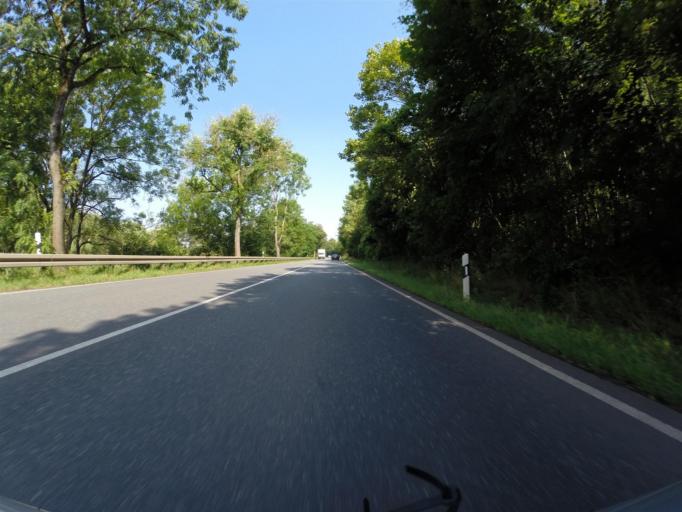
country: DE
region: Hesse
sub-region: Regierungsbezirk Kassel
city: Grossalmerode
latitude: 51.1862
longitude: 9.7965
